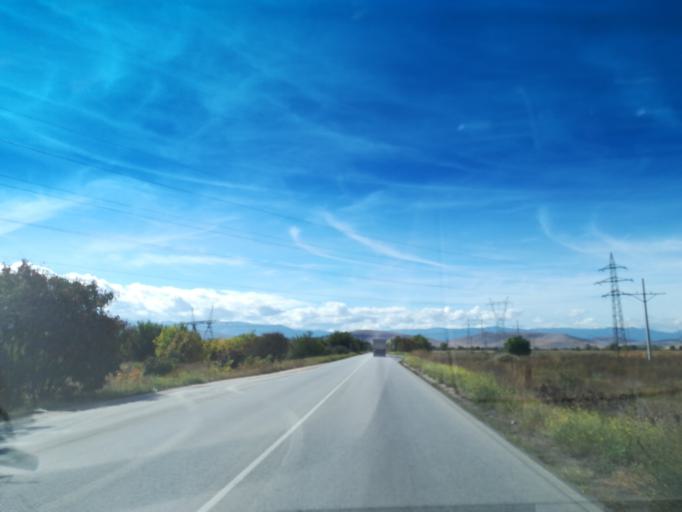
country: BG
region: Plovdiv
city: Stamboliyski
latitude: 42.1167
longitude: 24.5304
